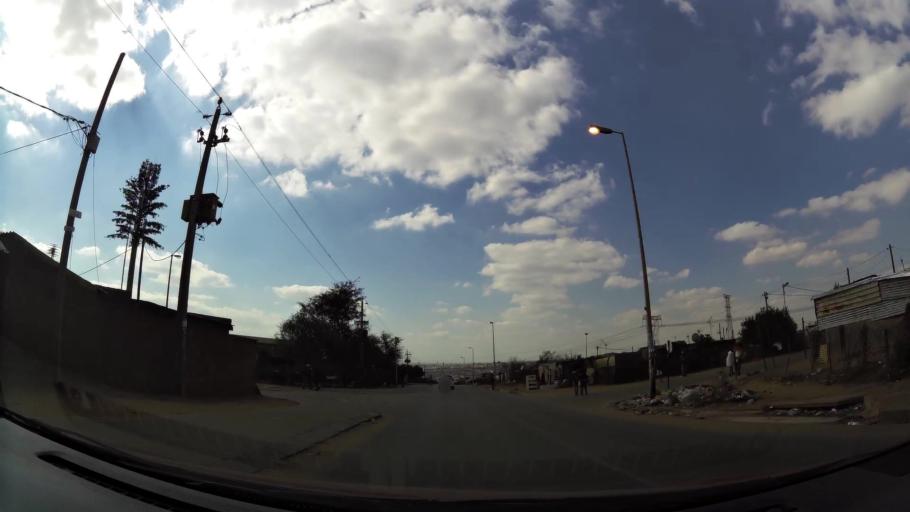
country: ZA
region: Gauteng
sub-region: Ekurhuleni Metropolitan Municipality
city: Tembisa
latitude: -26.0057
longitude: 28.1843
